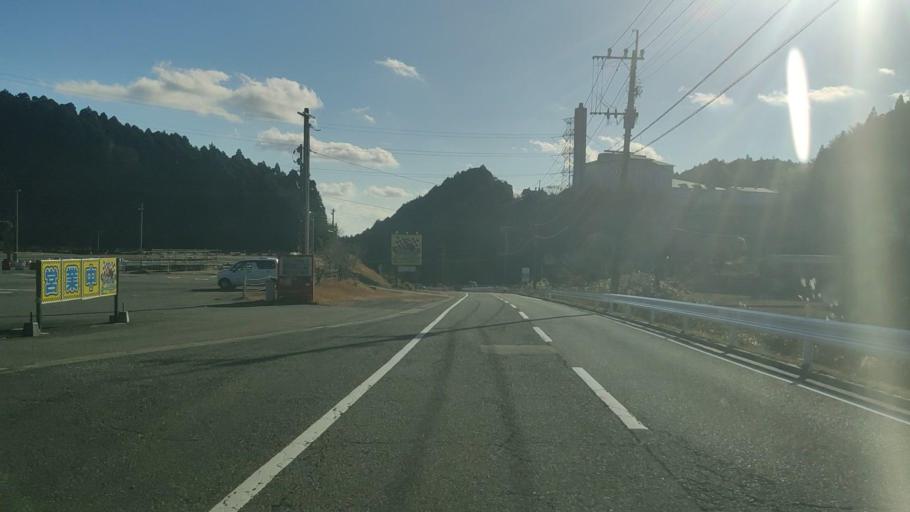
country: JP
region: Saga Prefecture
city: Kanzakimachi-kanzaki
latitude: 33.4005
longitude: 130.2721
